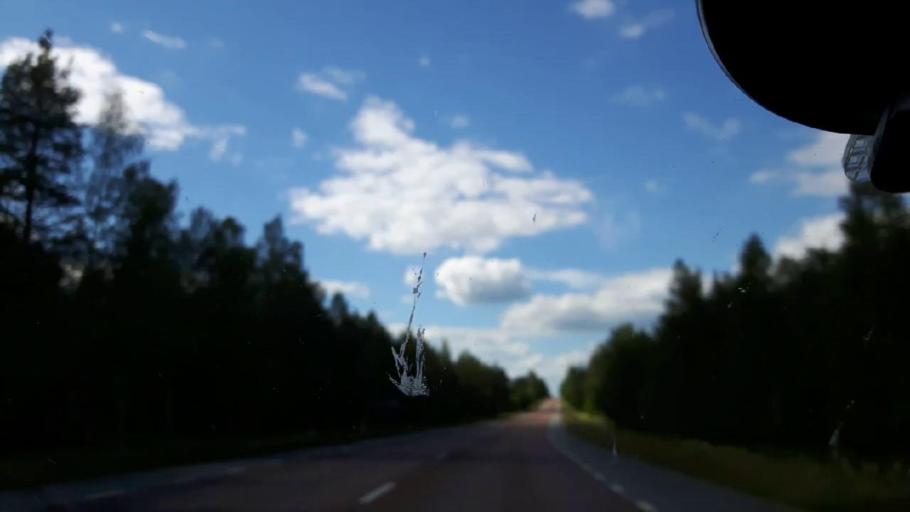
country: SE
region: Jaemtland
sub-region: Braecke Kommun
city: Braecke
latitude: 62.8205
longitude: 15.3323
